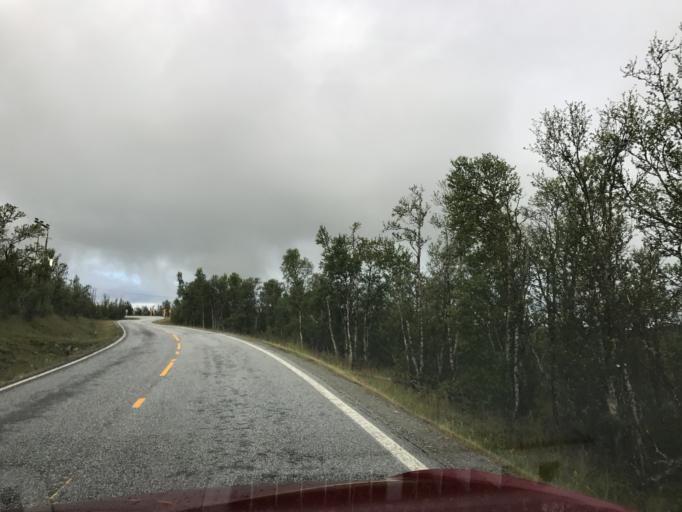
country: NO
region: Buskerud
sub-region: Hol
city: Hol
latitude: 60.4370
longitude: 8.3943
